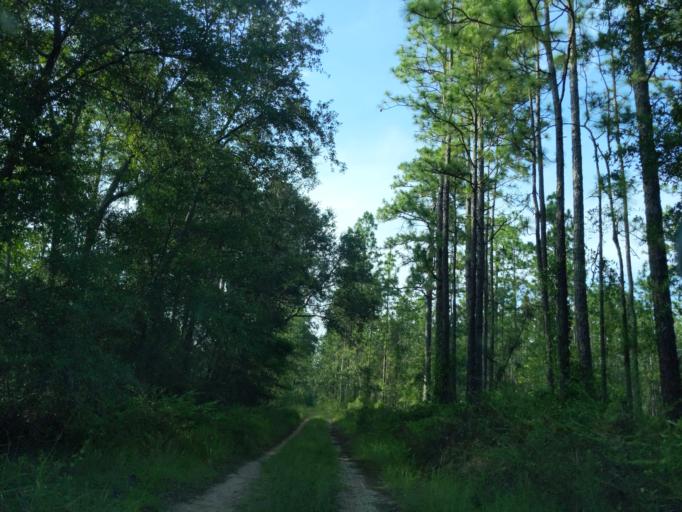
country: US
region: Florida
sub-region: Leon County
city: Tallahassee
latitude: 30.3555
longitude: -84.3611
